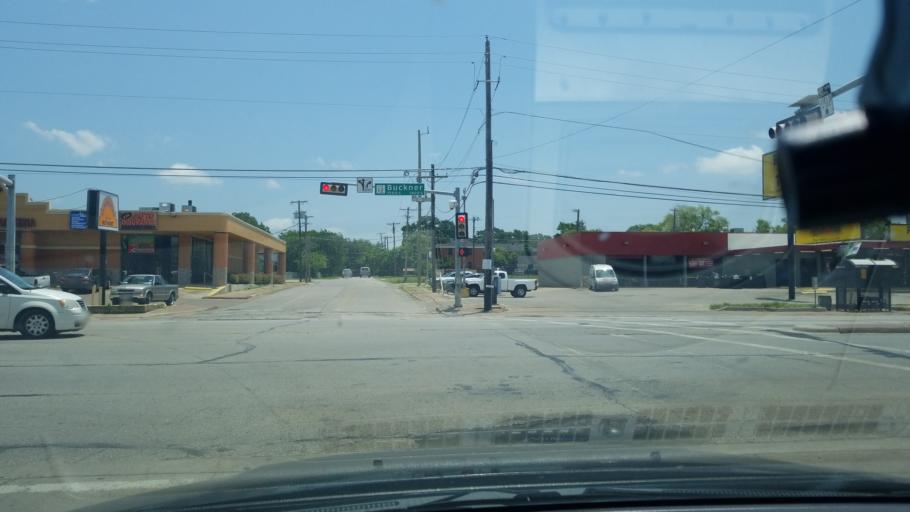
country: US
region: Texas
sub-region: Dallas County
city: Balch Springs
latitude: 32.7378
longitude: -96.6836
